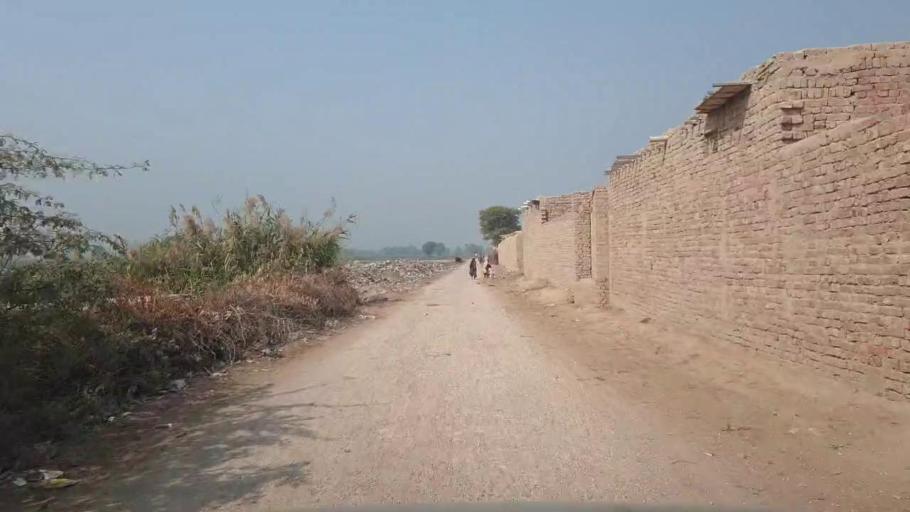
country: PK
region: Sindh
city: Hala
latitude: 25.8130
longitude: 68.4122
